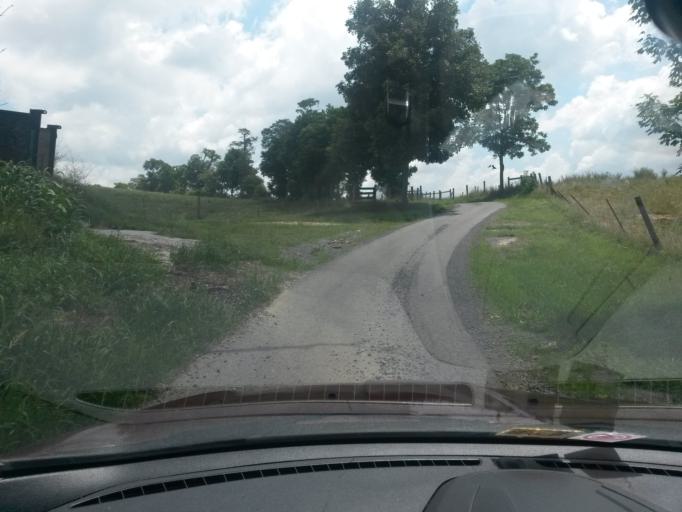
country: US
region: West Virginia
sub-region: Monroe County
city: Union
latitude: 37.5595
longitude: -80.5126
